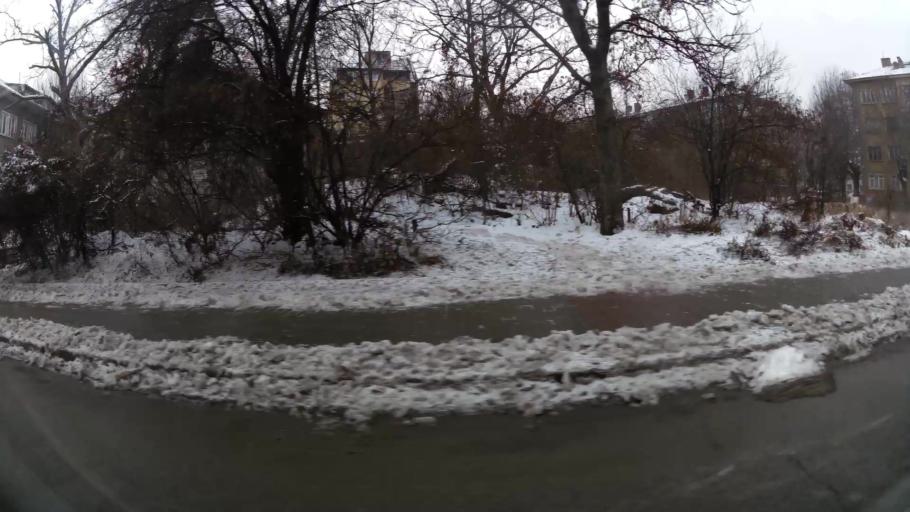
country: BG
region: Sofia-Capital
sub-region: Stolichna Obshtina
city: Sofia
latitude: 42.7120
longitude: 23.3174
